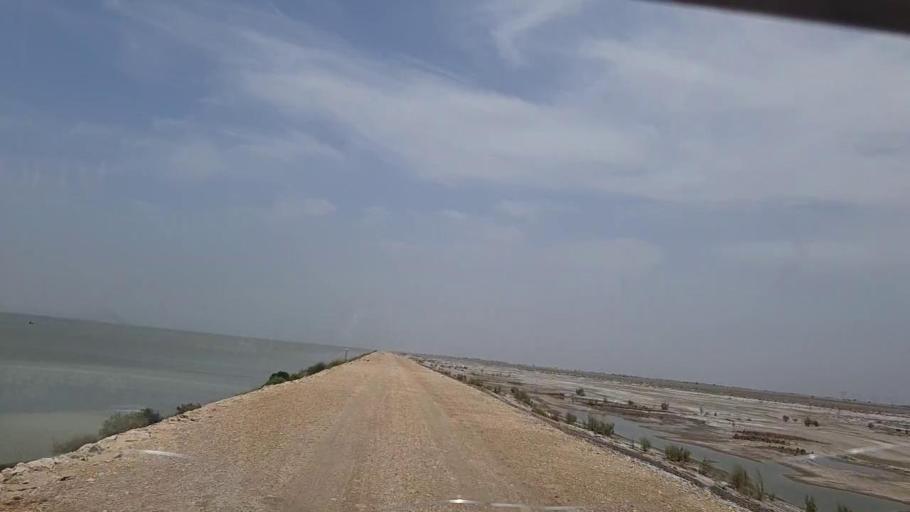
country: PK
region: Sindh
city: Sehwan
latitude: 26.4118
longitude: 67.7890
